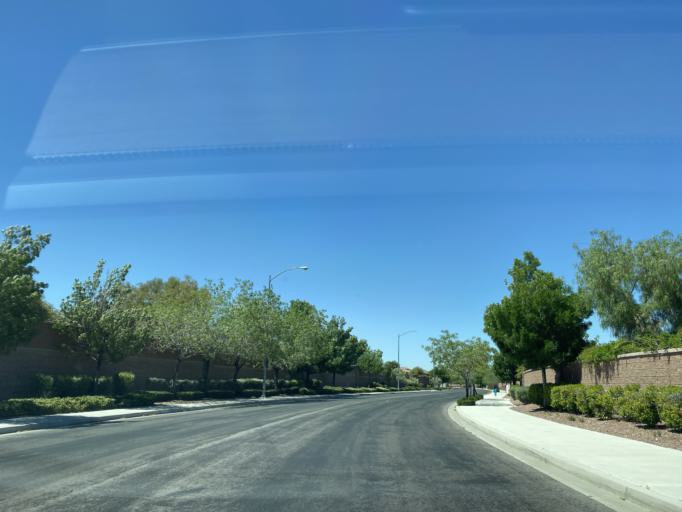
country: US
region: Nevada
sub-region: Clark County
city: Whitney
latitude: 35.9440
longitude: -115.0847
